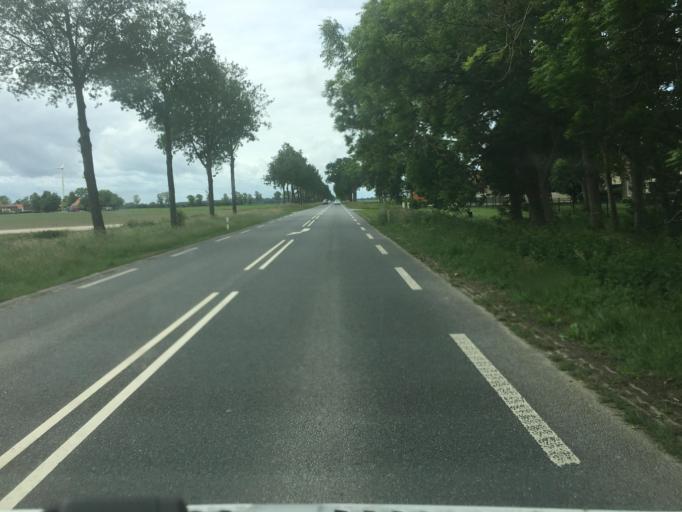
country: NL
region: Flevoland
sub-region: Gemeente Noordoostpolder
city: Emmeloord
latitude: 52.6736
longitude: 5.7501
